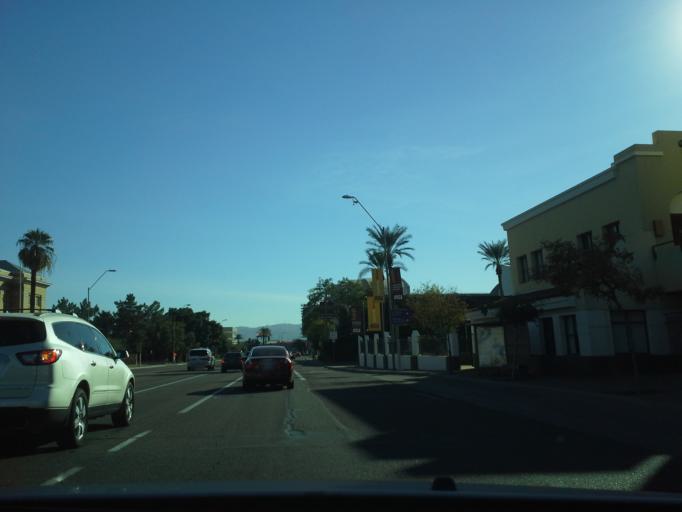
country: US
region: Arizona
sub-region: Maricopa County
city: Phoenix
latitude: 33.4511
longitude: -112.0652
